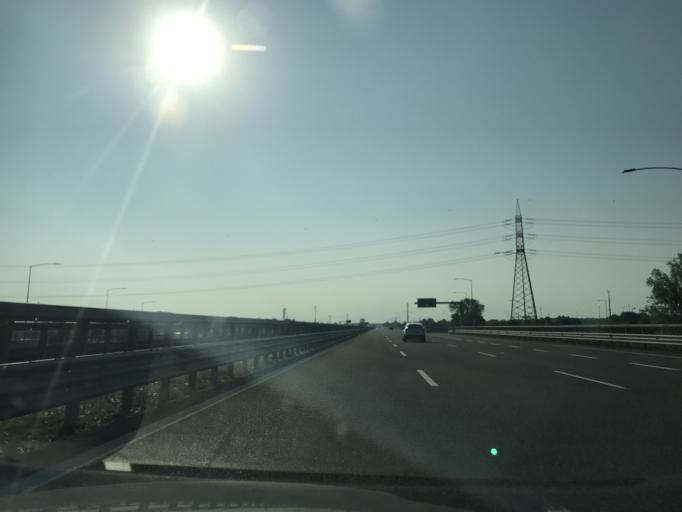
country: IT
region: Lombardy
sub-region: Provincia di Bergamo
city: Casirate d'Adda
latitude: 45.5090
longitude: 9.5486
